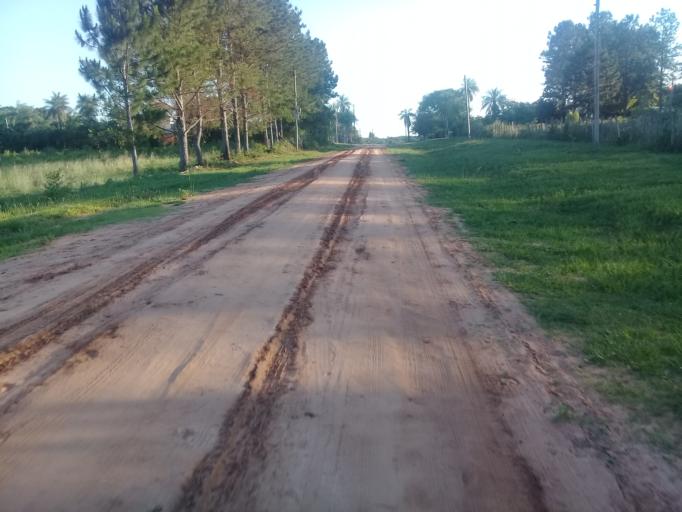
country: AR
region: Corrientes
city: San Luis del Palmar
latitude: -27.4710
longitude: -58.6639
